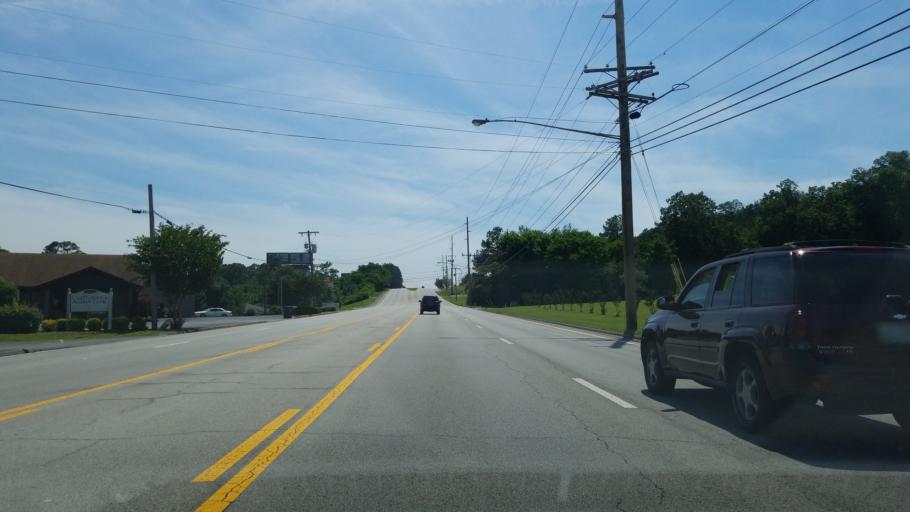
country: US
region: Tennessee
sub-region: Hamilton County
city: East Brainerd
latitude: 35.0376
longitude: -85.1742
